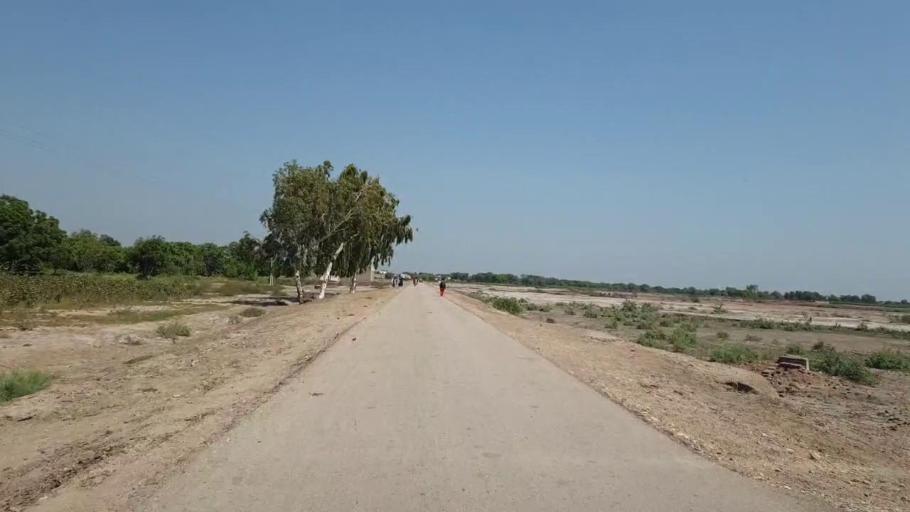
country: PK
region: Sindh
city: Hyderabad
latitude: 25.4455
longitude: 68.4111
